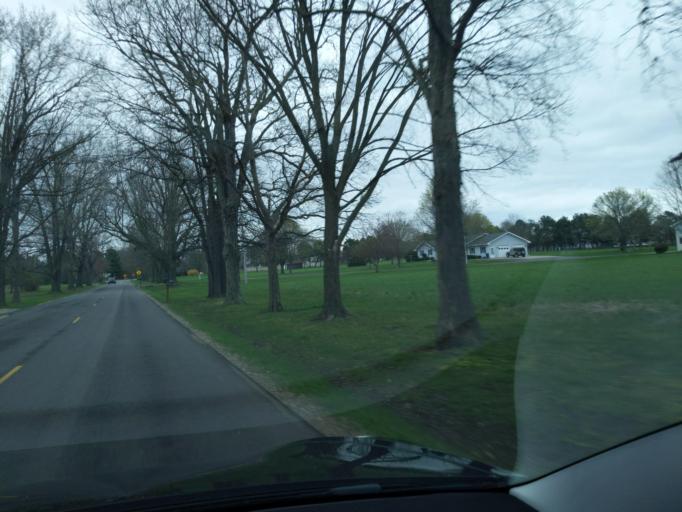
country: US
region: Michigan
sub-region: Ingham County
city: Stockbridge
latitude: 42.4508
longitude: -84.1506
